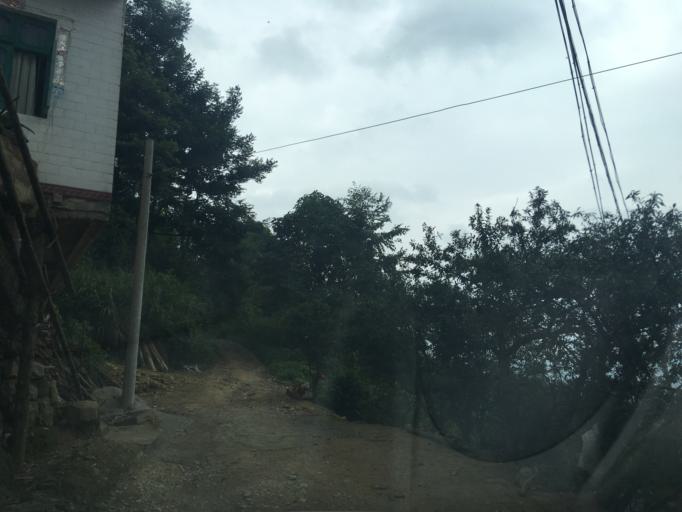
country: CN
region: Guangxi Zhuangzu Zizhiqu
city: Xinzhou
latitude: 25.1620
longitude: 105.6896
